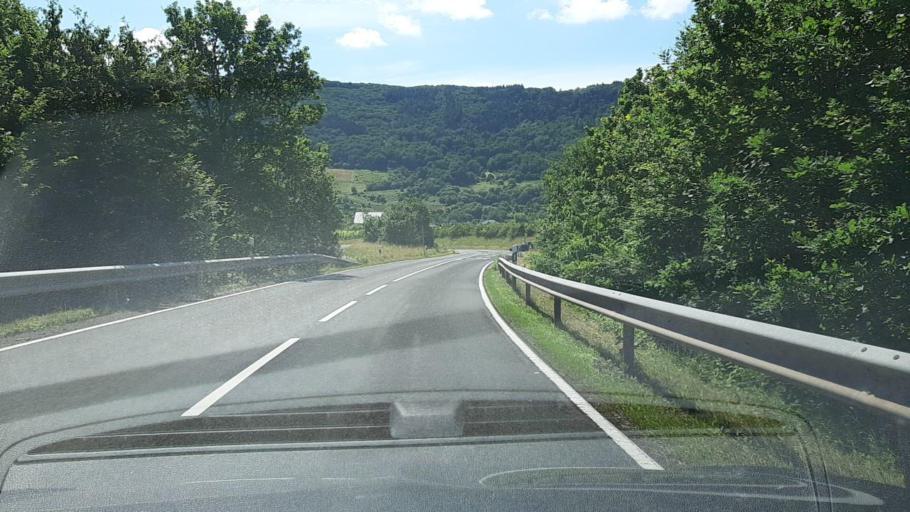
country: DE
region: Rheinland-Pfalz
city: Nehren
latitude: 50.0876
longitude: 7.1974
